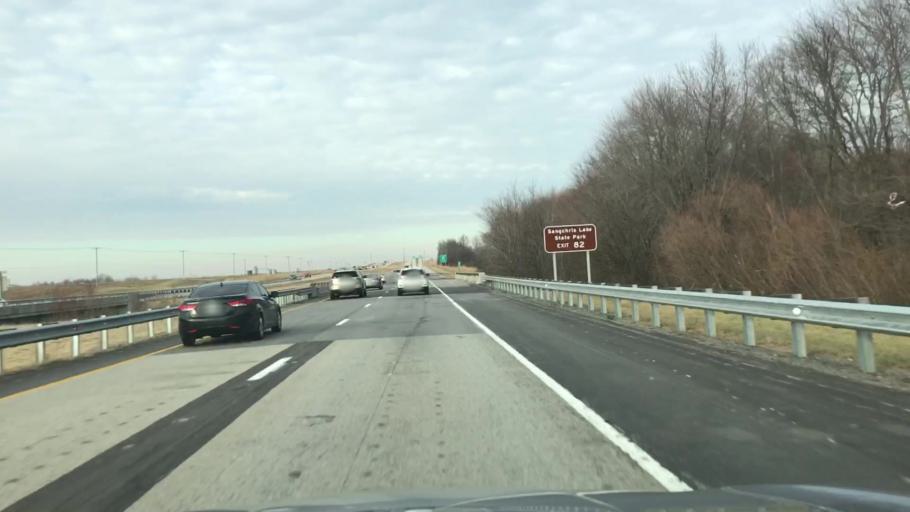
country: US
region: Illinois
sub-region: Sangamon County
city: Divernon
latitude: 39.5795
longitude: -89.6462
